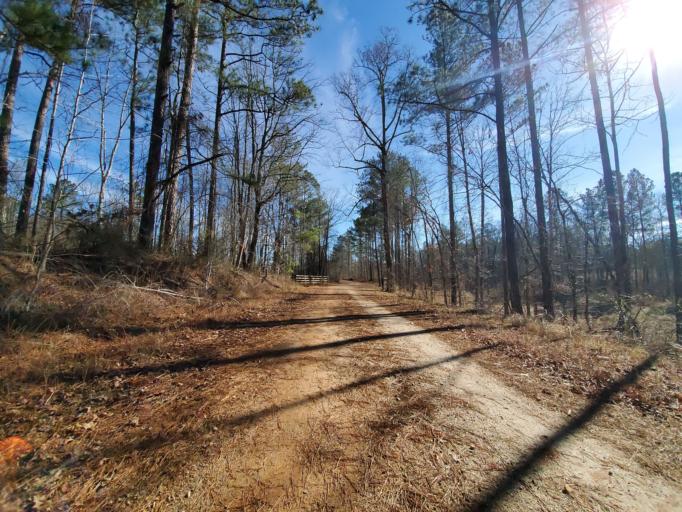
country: US
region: Georgia
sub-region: Fulton County
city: Chattahoochee Hills
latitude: 33.5698
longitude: -84.7560
